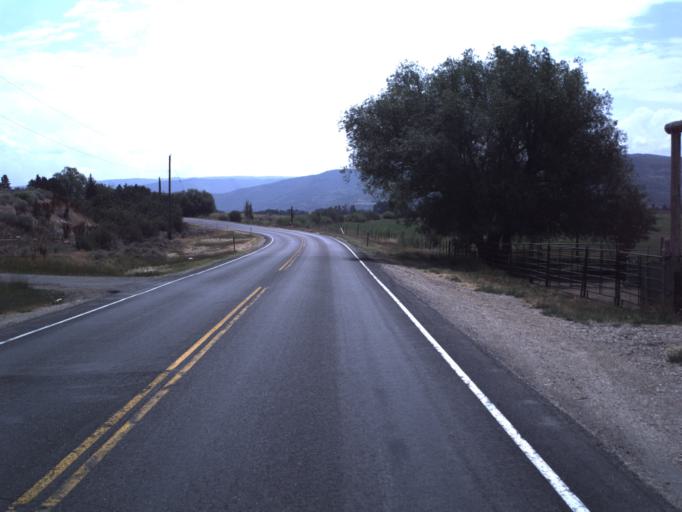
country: US
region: Utah
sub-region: Summit County
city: Francis
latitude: 40.6065
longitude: -111.2558
